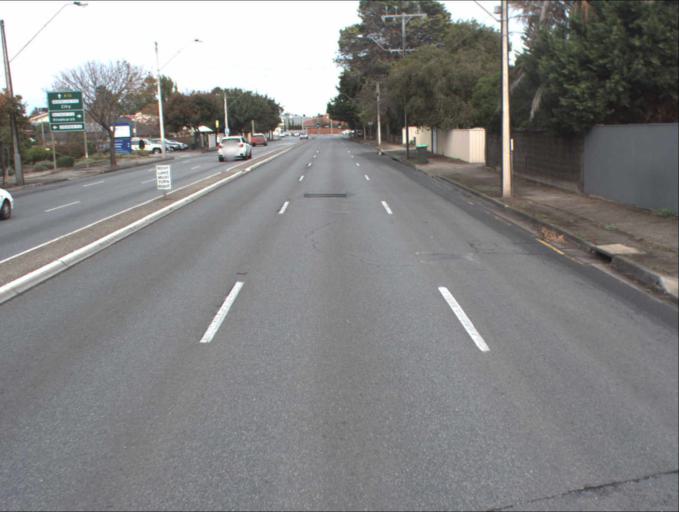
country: AU
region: South Australia
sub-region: Prospect
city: Prospect
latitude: -34.8912
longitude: 138.6113
